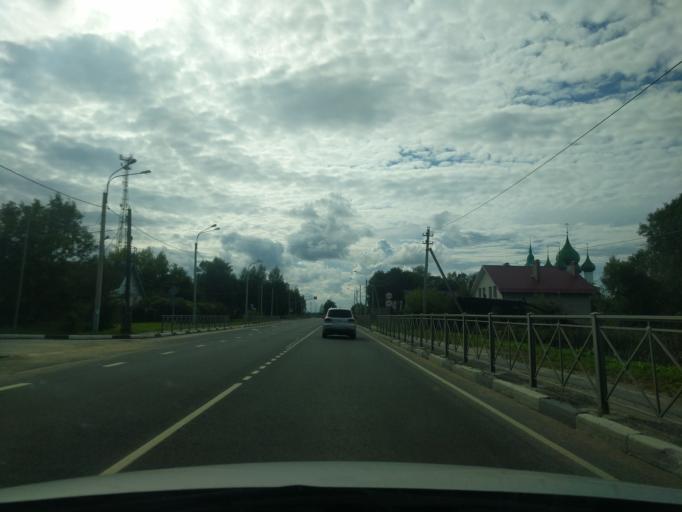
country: RU
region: Jaroslavl
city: Levashevo
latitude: 57.6439
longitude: 40.5314
